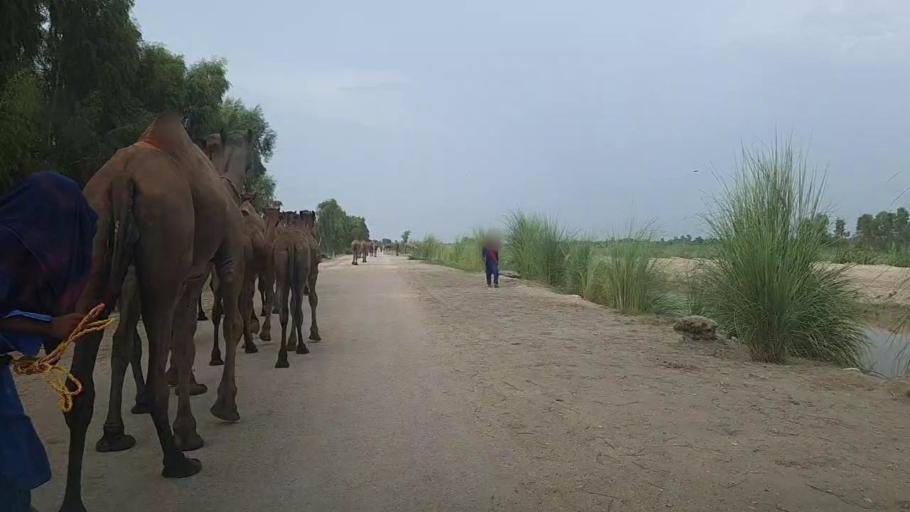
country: PK
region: Sindh
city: Karaundi
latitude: 26.9620
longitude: 68.4259
